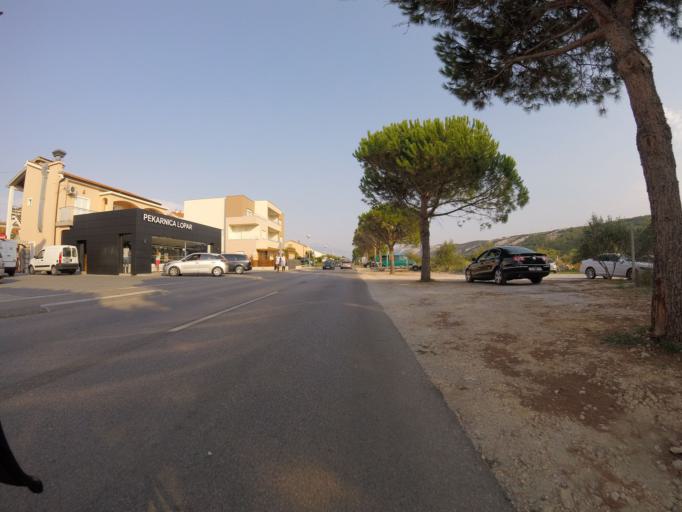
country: HR
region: Primorsko-Goranska
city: Lopar
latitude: 44.8289
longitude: 14.7330
